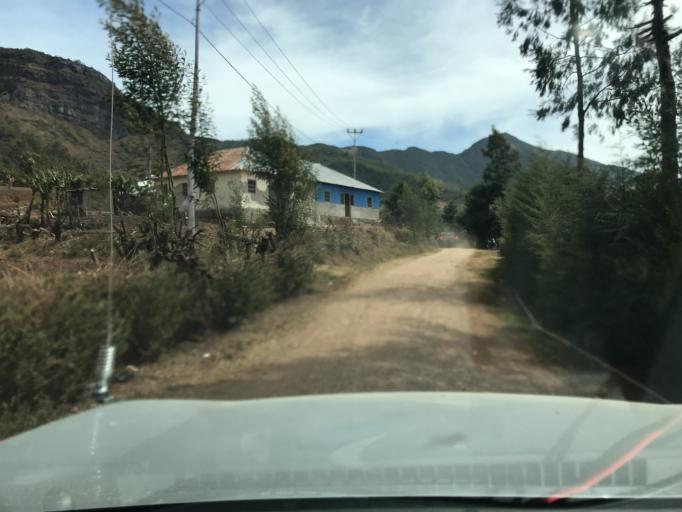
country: TL
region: Ainaro
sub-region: Ainaro
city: Ainaro
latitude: -8.8899
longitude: 125.5191
